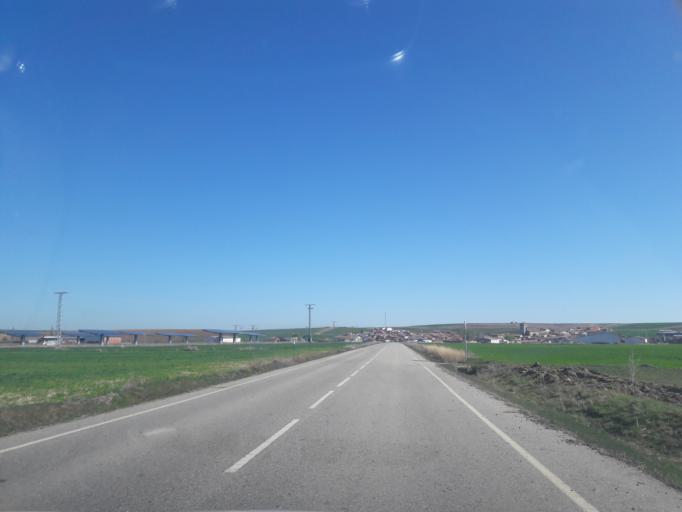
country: ES
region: Castille and Leon
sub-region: Provincia de Salamanca
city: Mancera de Abajo
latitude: 40.8336
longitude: -5.2052
